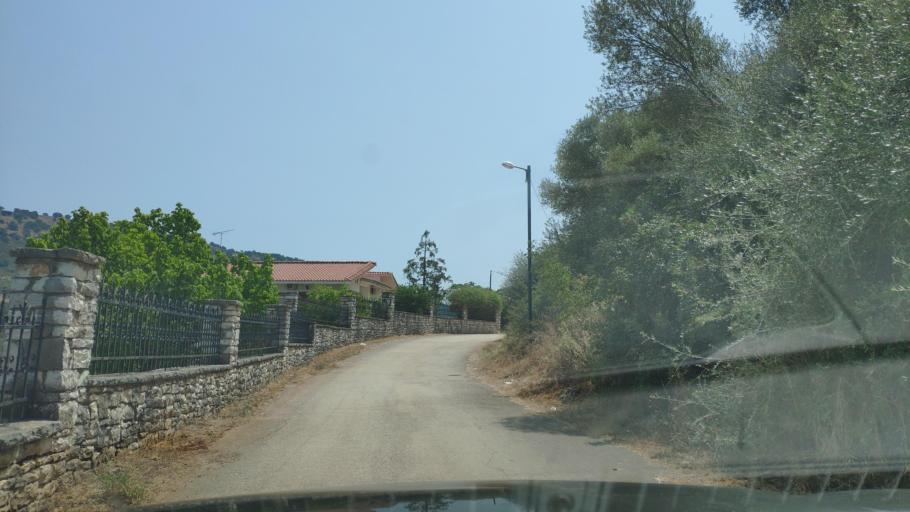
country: GR
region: West Greece
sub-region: Nomos Aitolias kai Akarnanias
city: Amfilochia
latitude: 38.8681
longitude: 21.0743
